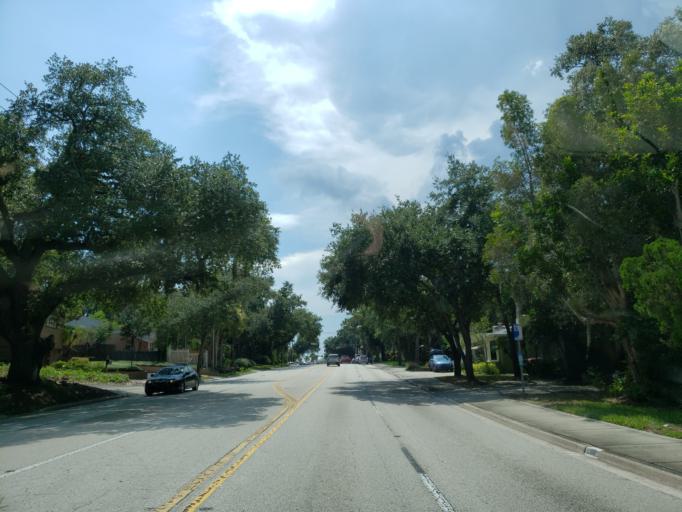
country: US
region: Florida
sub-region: Pinellas County
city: Lealman
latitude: 27.8067
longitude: -82.6451
